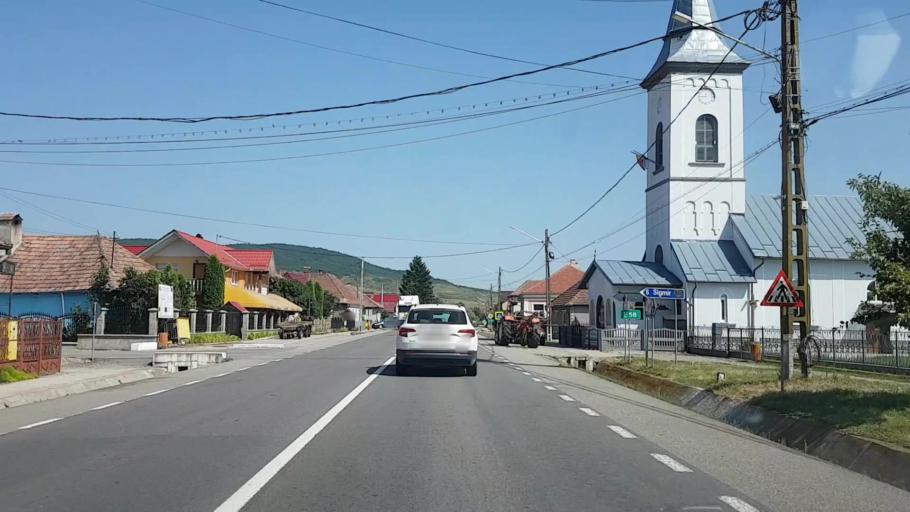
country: RO
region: Bistrita-Nasaud
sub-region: Comuna Sieu-Magherus
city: Sieu-Magherus
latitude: 47.0896
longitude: 24.3760
